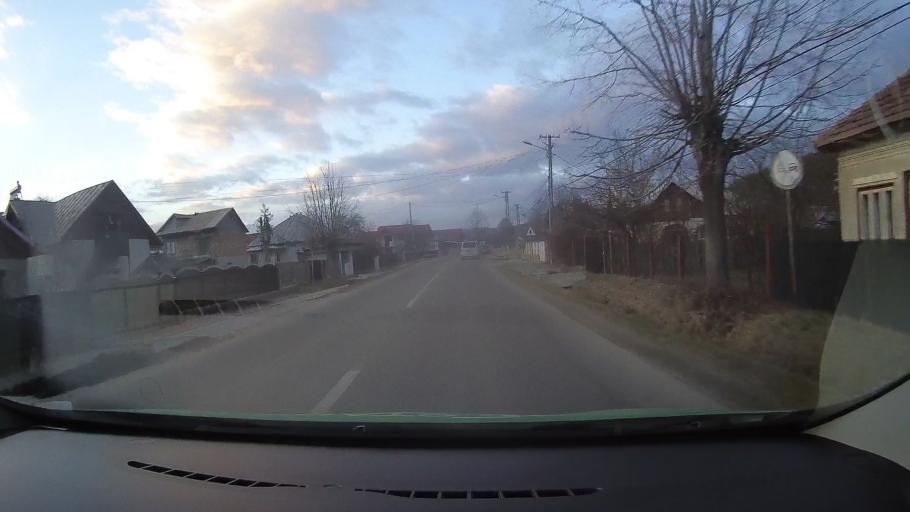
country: RO
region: Dambovita
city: Iedera de Jos
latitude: 45.0220
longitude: 25.6365
